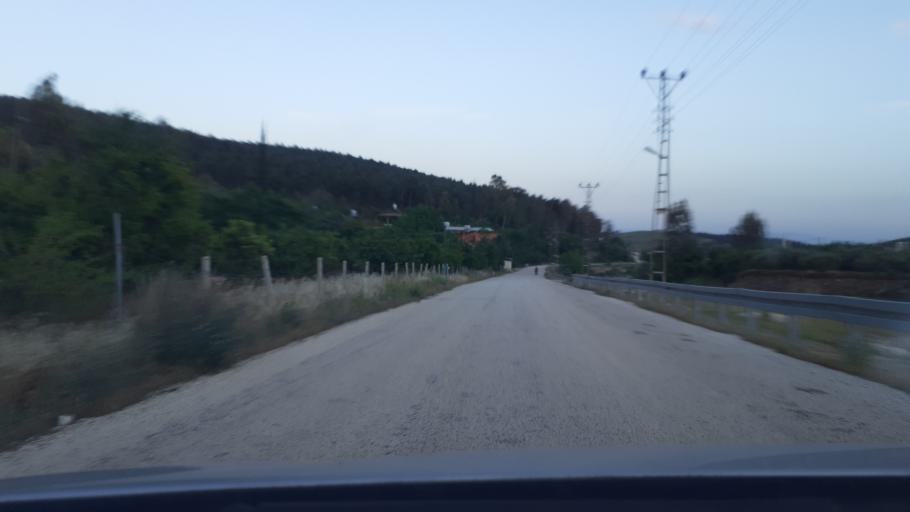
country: TR
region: Hatay
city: Kirikhan
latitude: 36.5091
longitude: 36.3211
